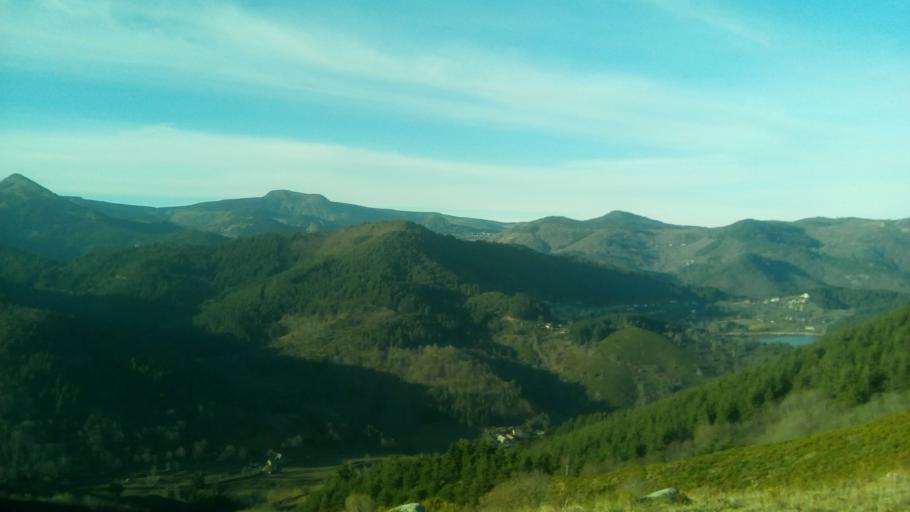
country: FR
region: Rhone-Alpes
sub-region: Departement de l'Ardeche
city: Le Chambon
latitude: 44.8496
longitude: 4.2879
